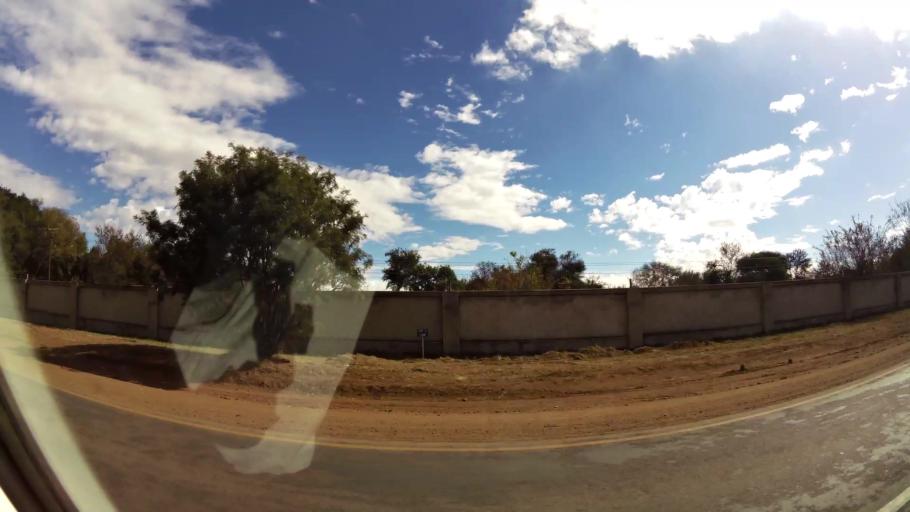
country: ZA
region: Limpopo
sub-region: Waterberg District Municipality
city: Bela-Bela
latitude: -24.8650
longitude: 28.3270
